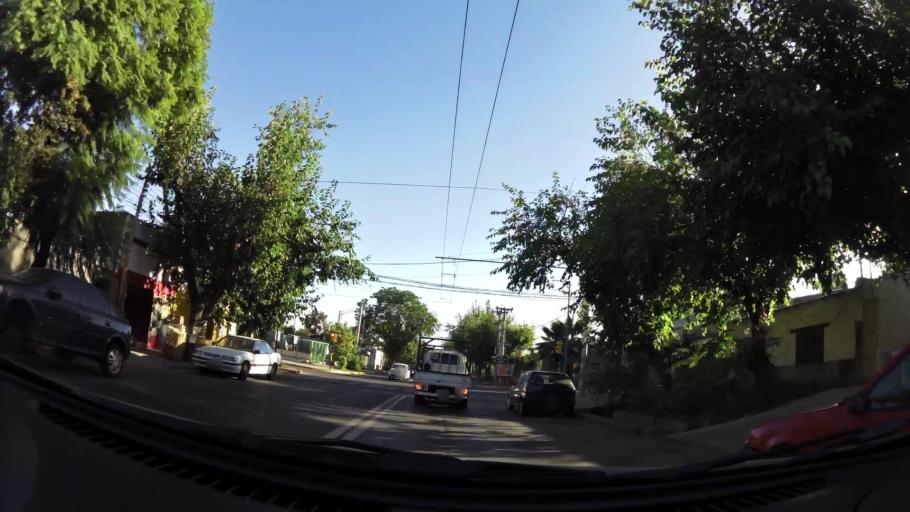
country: AR
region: Mendoza
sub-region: Departamento de Godoy Cruz
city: Godoy Cruz
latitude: -32.9419
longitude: -68.8482
